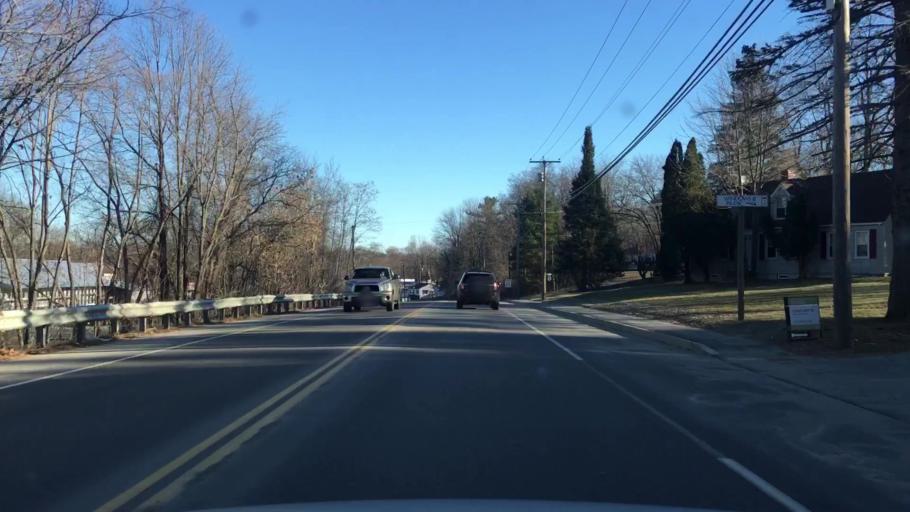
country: US
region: Maine
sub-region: Kennebec County
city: Winslow
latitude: 44.5358
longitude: -69.6321
